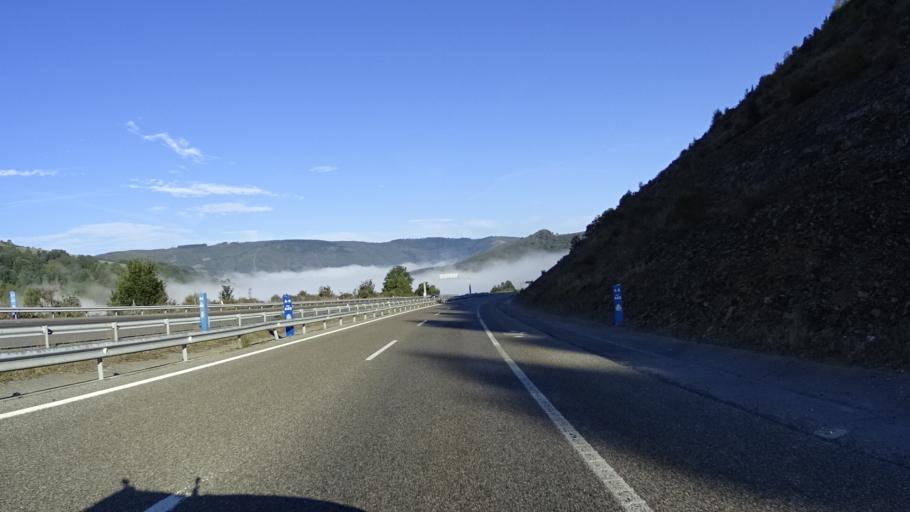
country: ES
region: Galicia
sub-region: Provincia de Lugo
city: San Roman
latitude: 42.7738
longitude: -7.0944
